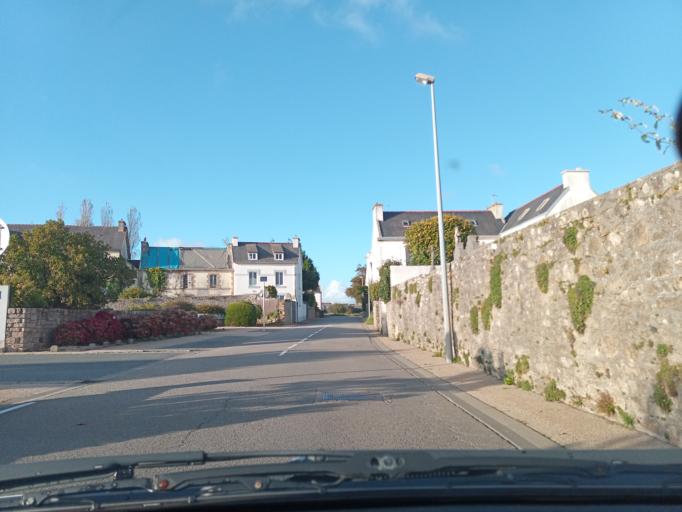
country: FR
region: Brittany
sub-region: Departement du Finistere
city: Esquibien
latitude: 48.0262
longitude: -4.5615
